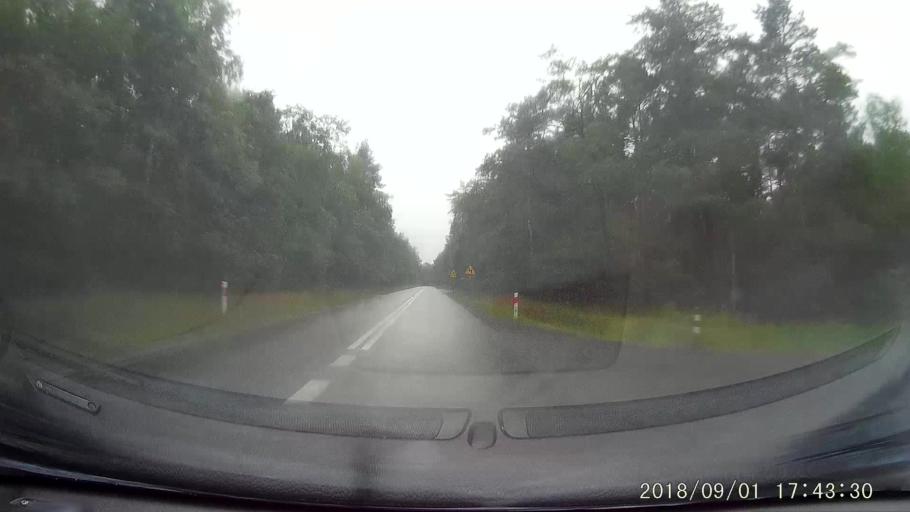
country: PL
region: Lubusz
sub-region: Powiat zaganski
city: Ilowa
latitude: 51.5436
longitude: 15.2490
